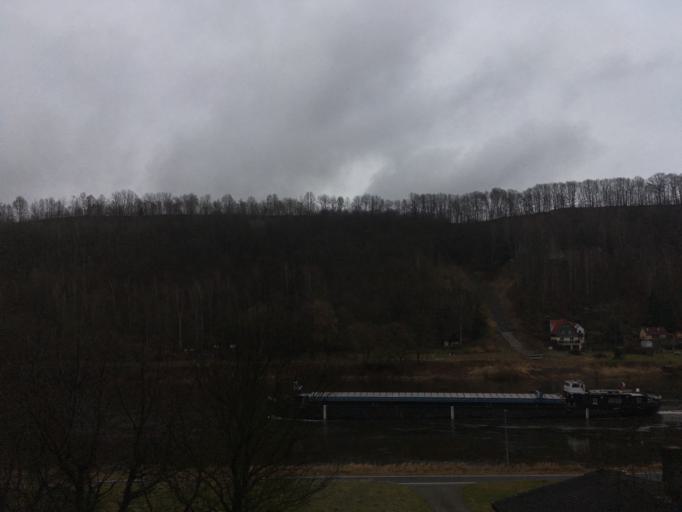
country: DE
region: Saxony
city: Struppen
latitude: 50.9484
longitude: 13.9927
